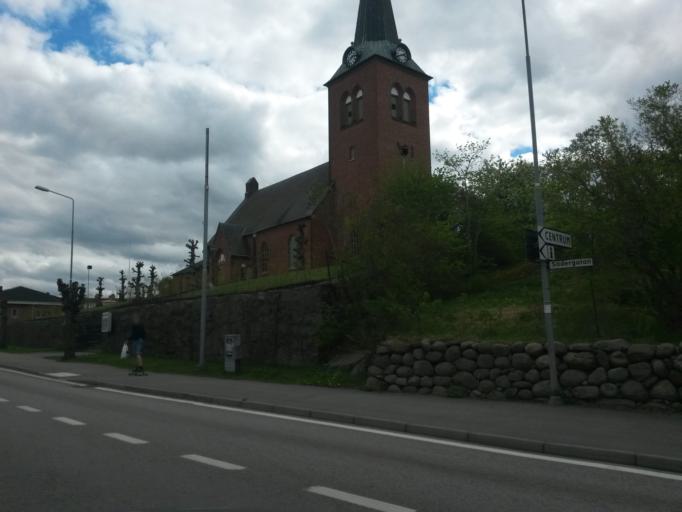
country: SE
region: Vaestra Goetaland
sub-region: Grastorps Kommun
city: Graestorp
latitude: 58.3333
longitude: 12.6807
